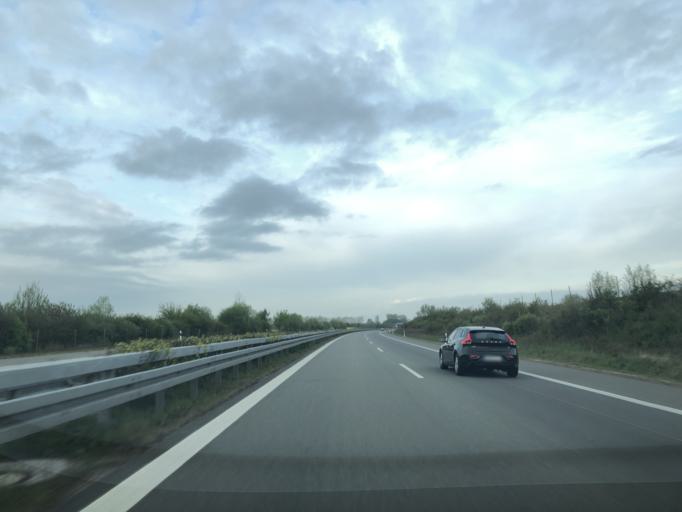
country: DE
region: Mecklenburg-Vorpommern
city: Franzburg
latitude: 54.0747
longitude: 12.9203
